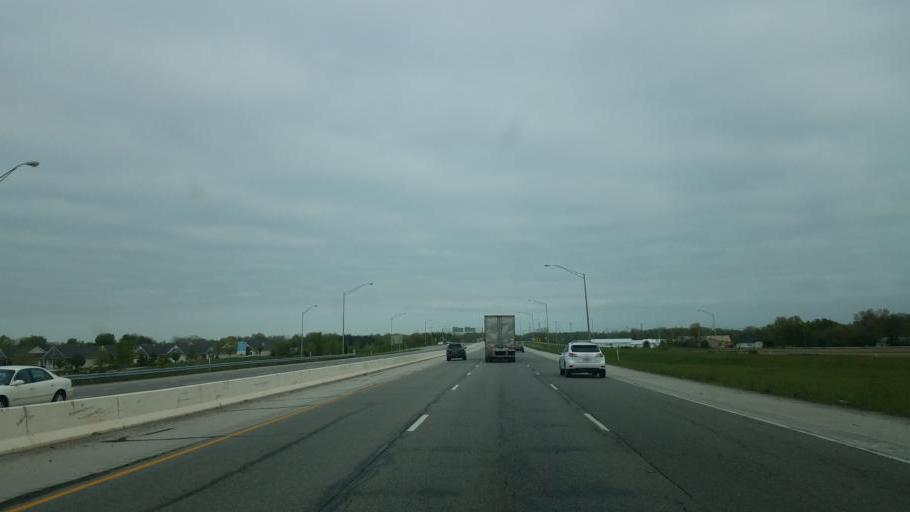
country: US
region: Indiana
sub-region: Allen County
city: Leo-Cedarville
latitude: 41.1602
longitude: -85.0642
